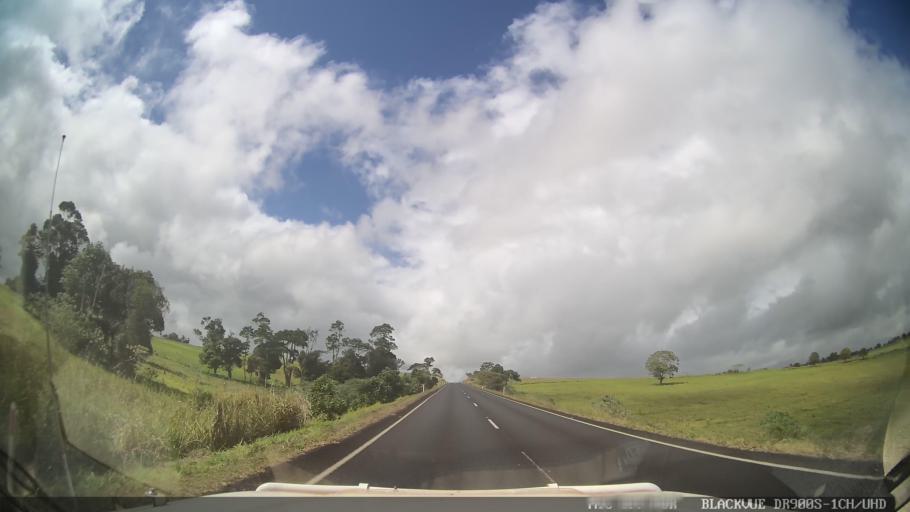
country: AU
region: Queensland
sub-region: Tablelands
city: Atherton
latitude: -17.2961
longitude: 145.6184
